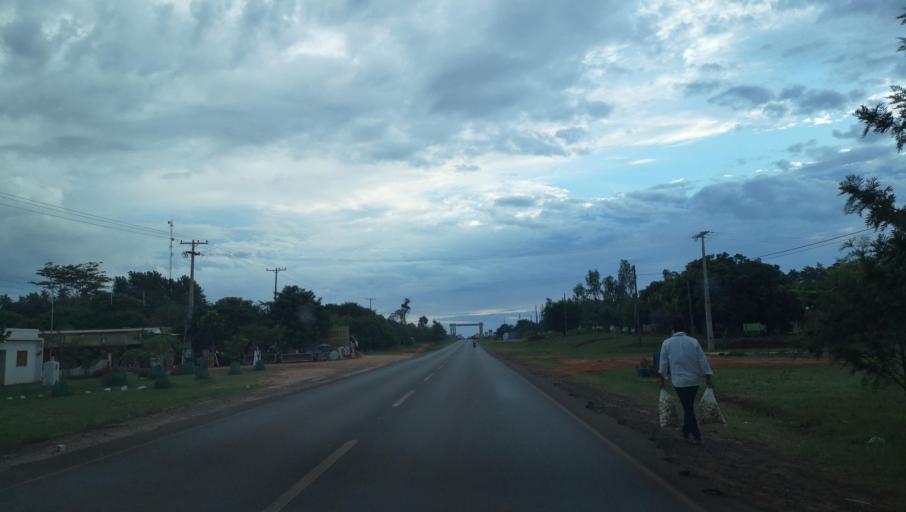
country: PY
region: San Pedro
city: Capiibary
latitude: -24.7148
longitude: -56.0128
